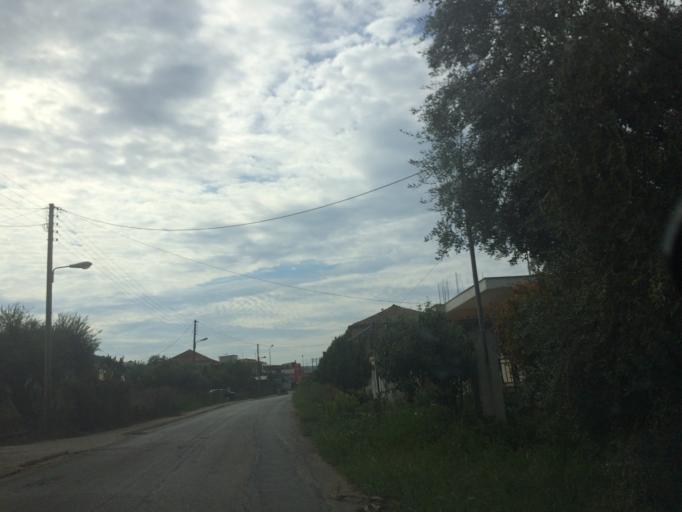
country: GR
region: Peloponnese
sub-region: Nomos Messinias
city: Pylos
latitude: 36.9602
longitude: 21.7009
